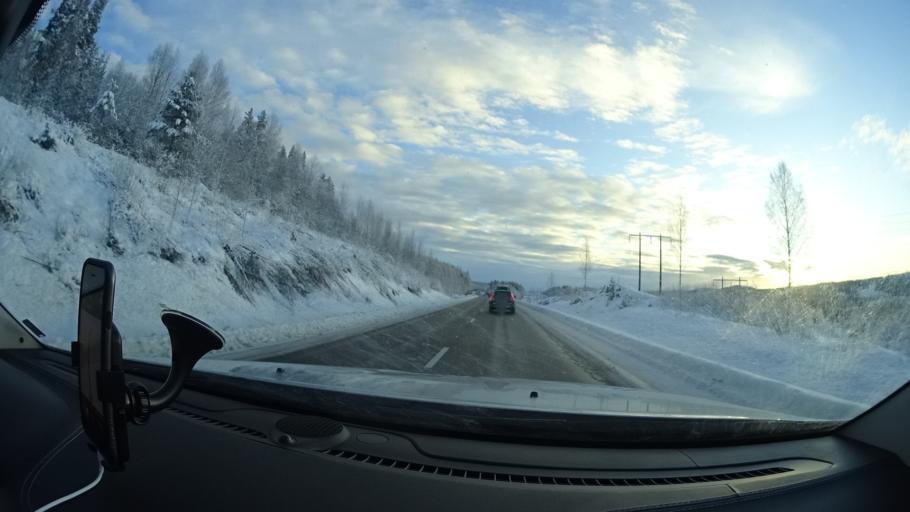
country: SE
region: Jaemtland
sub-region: Ragunda Kommun
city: Hammarstrand
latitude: 63.0719
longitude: 16.4967
